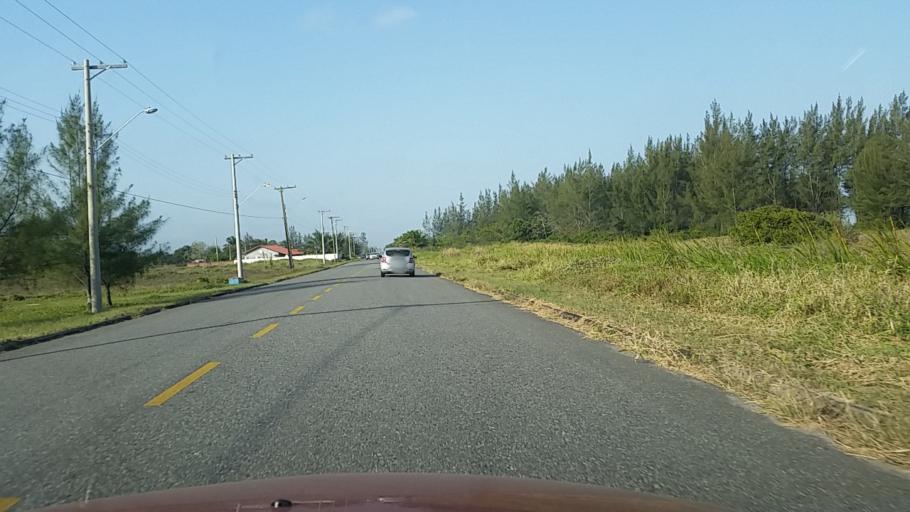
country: BR
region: Sao Paulo
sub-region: Iguape
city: Iguape
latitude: -24.7861
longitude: -47.6090
